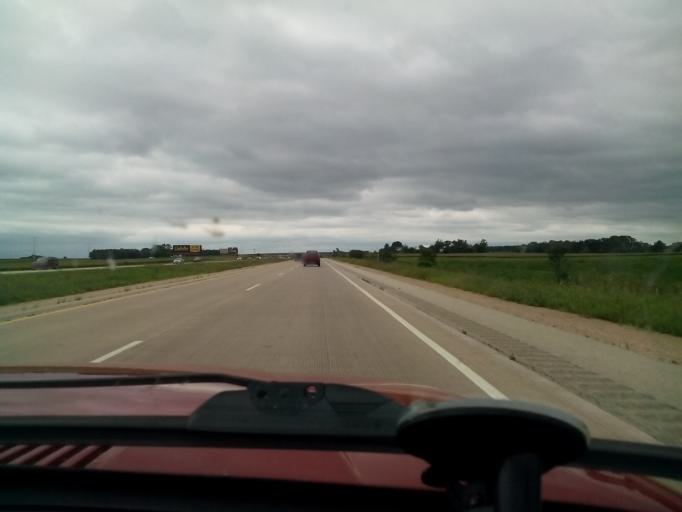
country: US
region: Wisconsin
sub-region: Columbia County
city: Columbus
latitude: 43.3330
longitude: -89.0448
